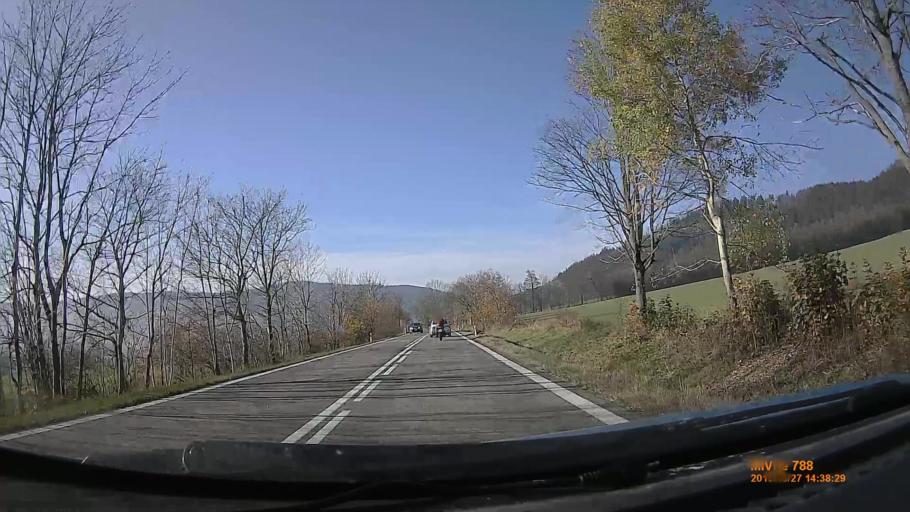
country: CZ
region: Olomoucky
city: Stity
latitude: 49.9963
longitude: 16.7712
